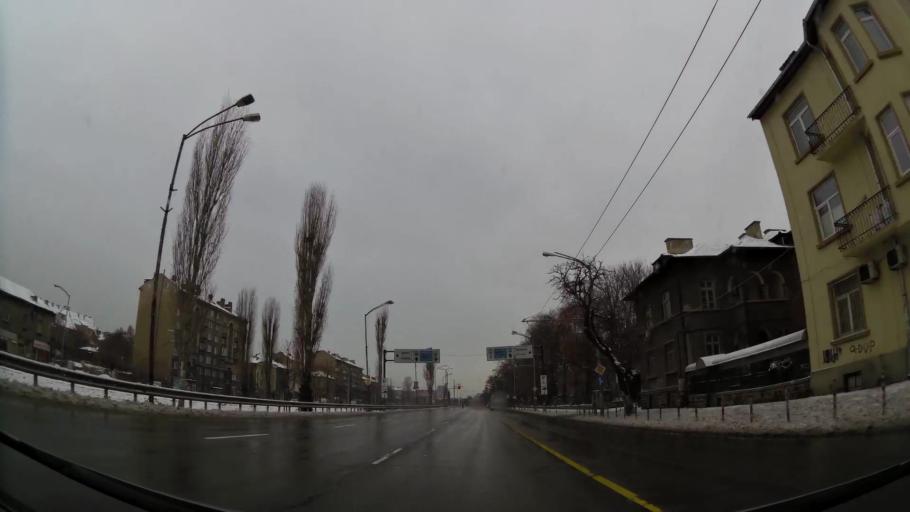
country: BG
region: Sofia-Capital
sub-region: Stolichna Obshtina
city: Sofia
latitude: 42.7054
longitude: 23.3197
